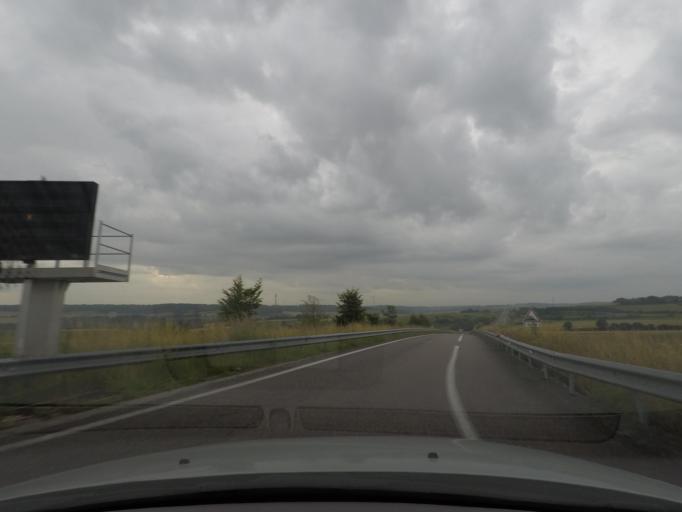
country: FR
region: Haute-Normandie
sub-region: Departement de la Seine-Maritime
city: Neufchatel-en-Bray
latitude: 49.7436
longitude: 1.5292
